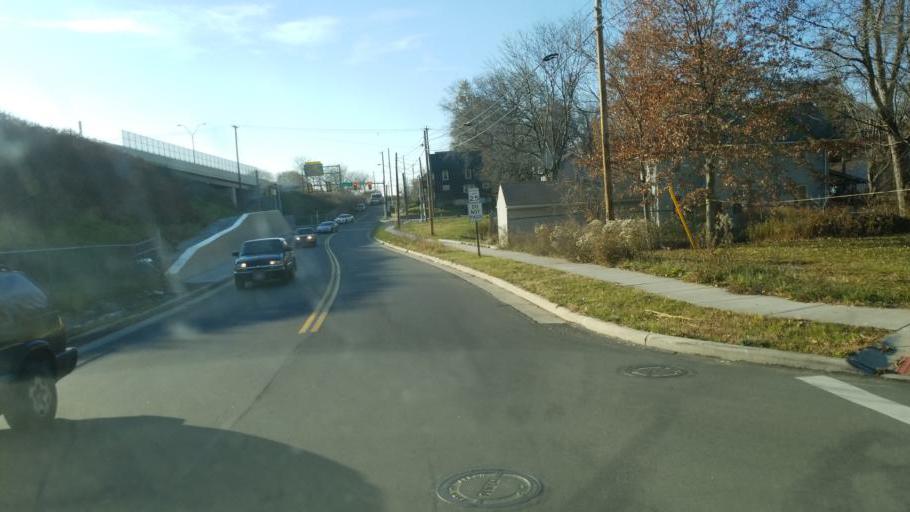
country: US
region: Ohio
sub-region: Summit County
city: Akron
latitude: 41.0629
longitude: -81.5085
